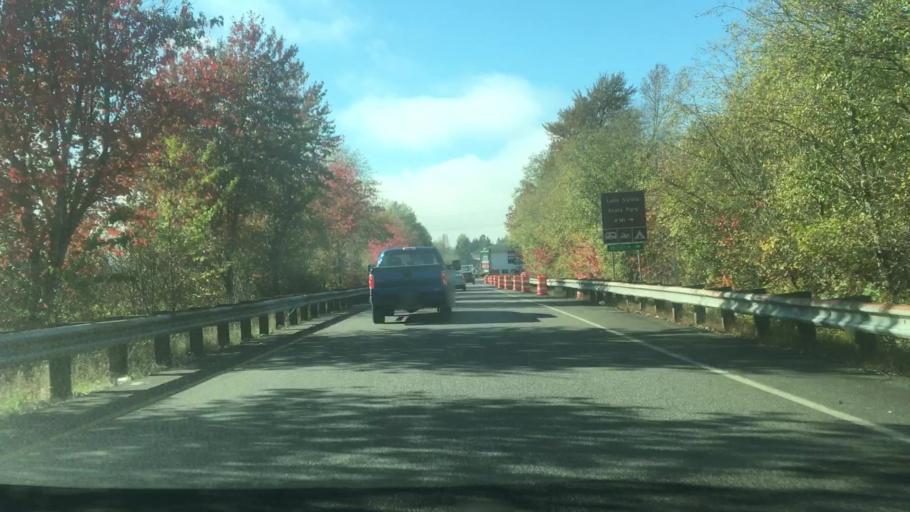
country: US
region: Washington
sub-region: Grays Harbor County
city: Montesano
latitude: 46.9771
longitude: -123.5982
